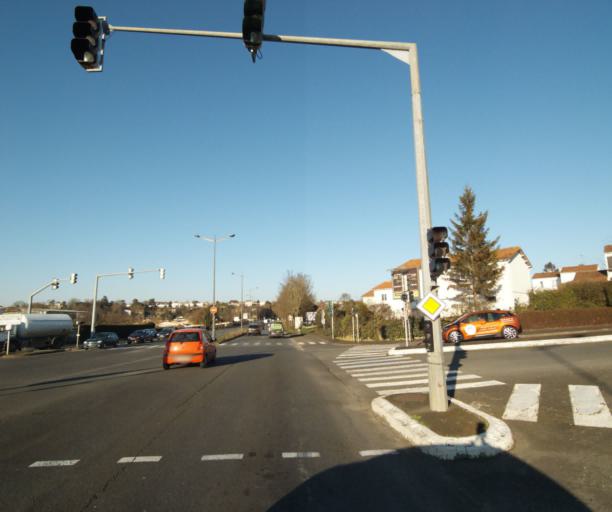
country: FR
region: Poitou-Charentes
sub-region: Departement des Deux-Sevres
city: Niort
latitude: 46.3313
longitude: -0.4828
